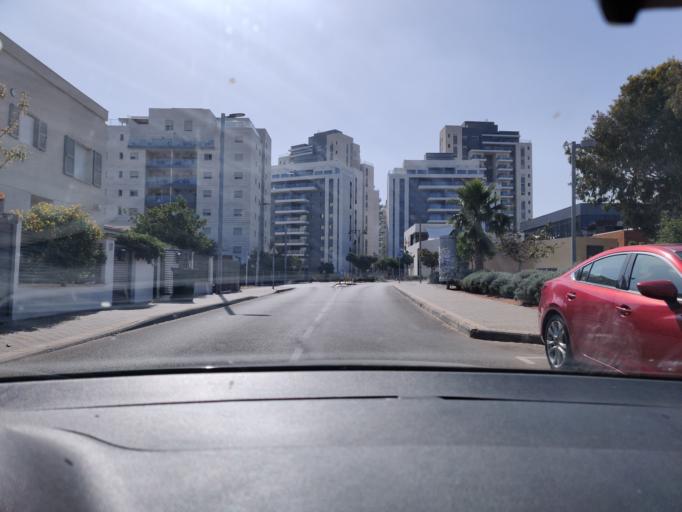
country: IL
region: Haifa
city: Hadera
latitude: 32.4682
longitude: 34.9516
